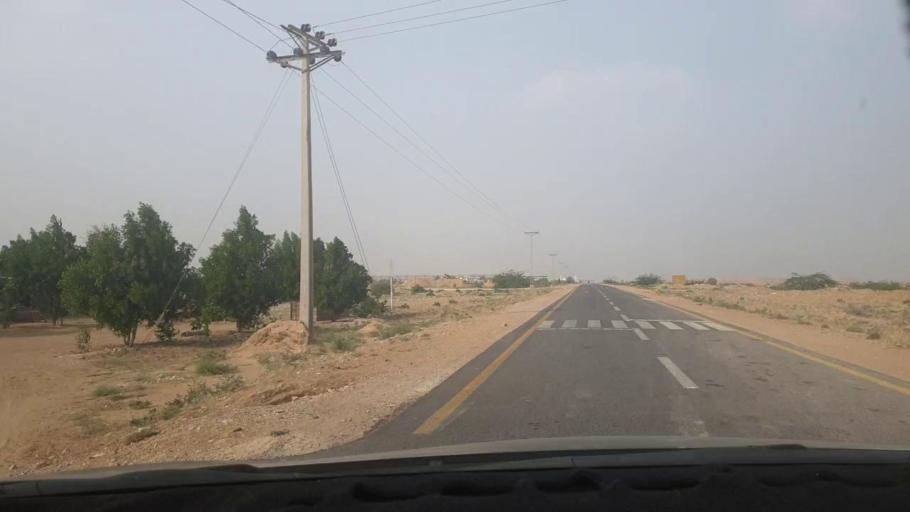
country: PK
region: Sindh
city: Jamshoro
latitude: 25.5651
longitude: 68.3171
